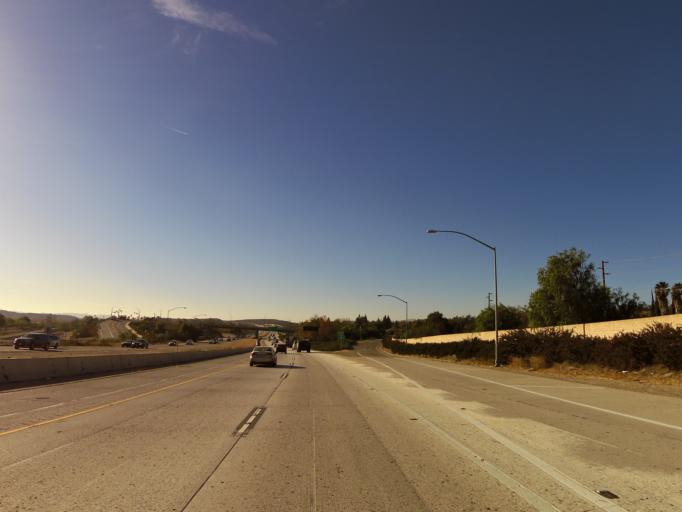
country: US
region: California
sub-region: Ventura County
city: Moorpark
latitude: 34.2936
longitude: -118.8385
